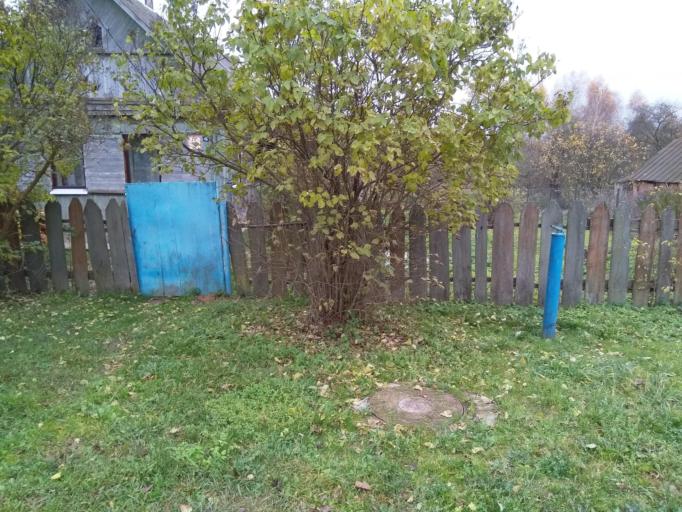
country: BY
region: Mogilev
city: Mahilyow
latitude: 53.9296
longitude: 30.3985
